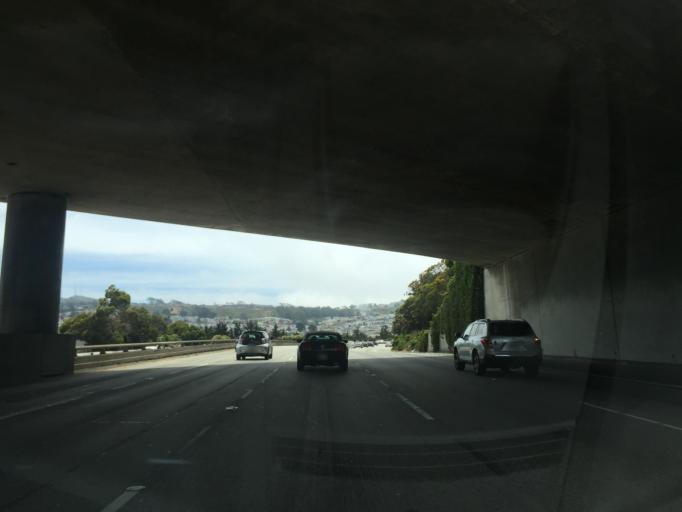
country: US
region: California
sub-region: San Mateo County
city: Daly City
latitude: 37.7188
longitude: -122.4486
